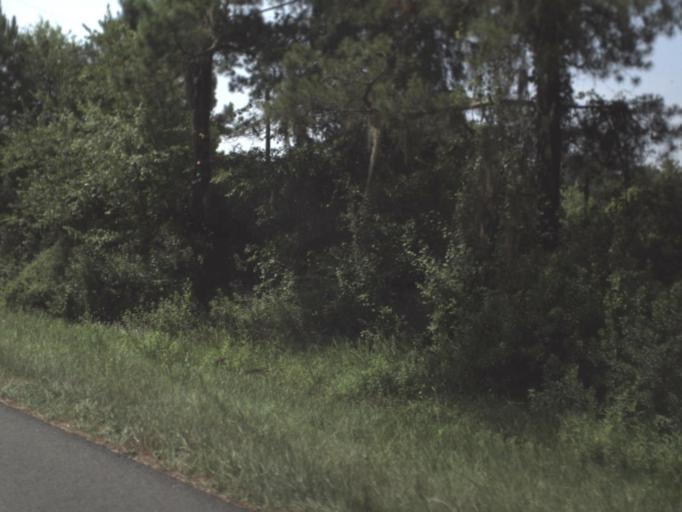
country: US
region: Florida
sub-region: Hamilton County
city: Jasper
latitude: 30.5286
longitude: -82.9674
